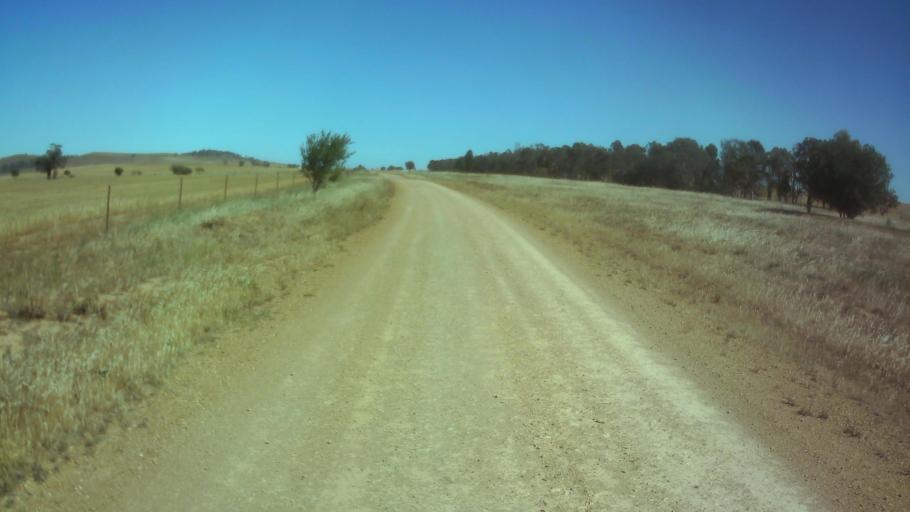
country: AU
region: New South Wales
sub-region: Weddin
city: Grenfell
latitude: -33.9705
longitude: 148.3173
